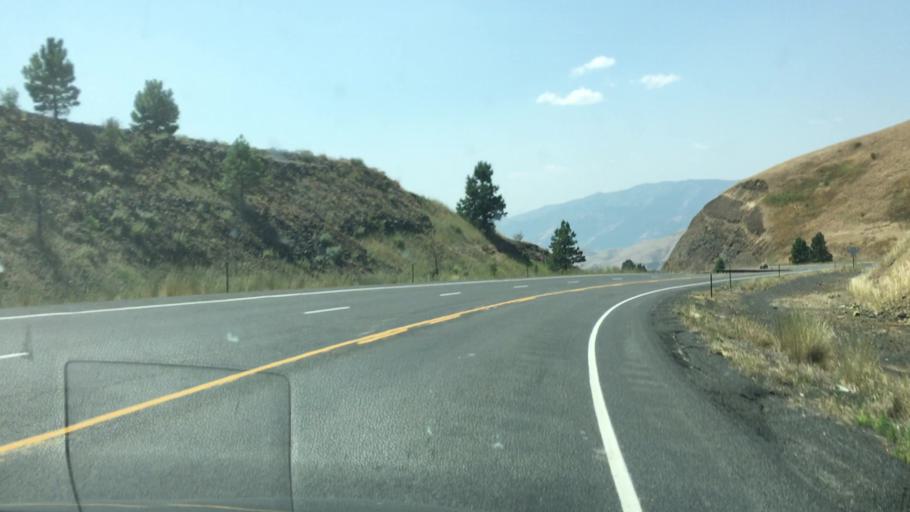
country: US
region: Idaho
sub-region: Idaho County
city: Grangeville
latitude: 45.8328
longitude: -116.2410
